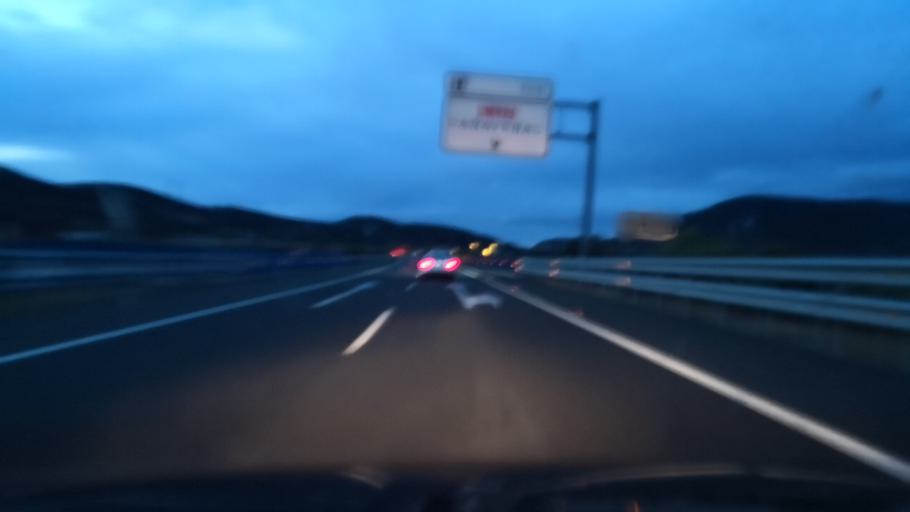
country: ES
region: Extremadura
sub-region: Provincia de Caceres
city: Canaveral
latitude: 39.7935
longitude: -6.3673
